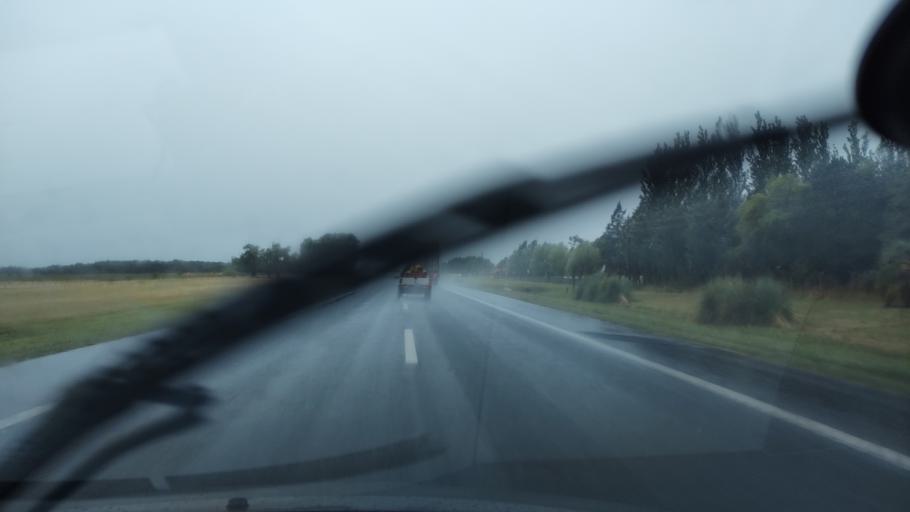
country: AR
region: Buenos Aires
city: Canuelas
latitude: -35.0630
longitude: -58.8158
